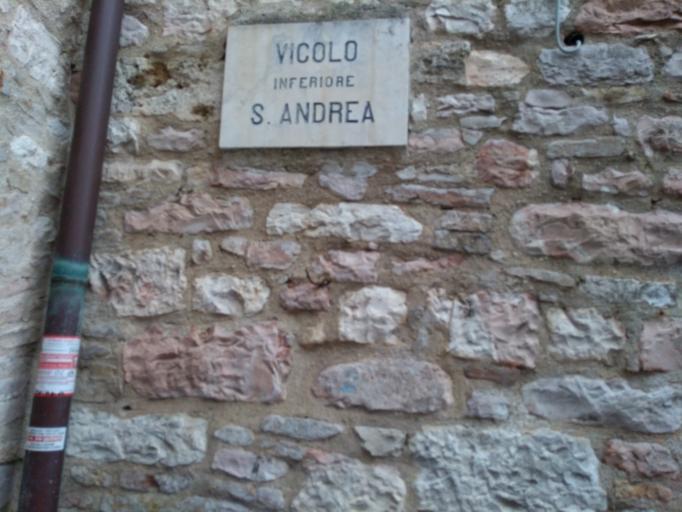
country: IT
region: Umbria
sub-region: Provincia di Perugia
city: Assisi
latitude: 43.0742
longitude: 12.6083
